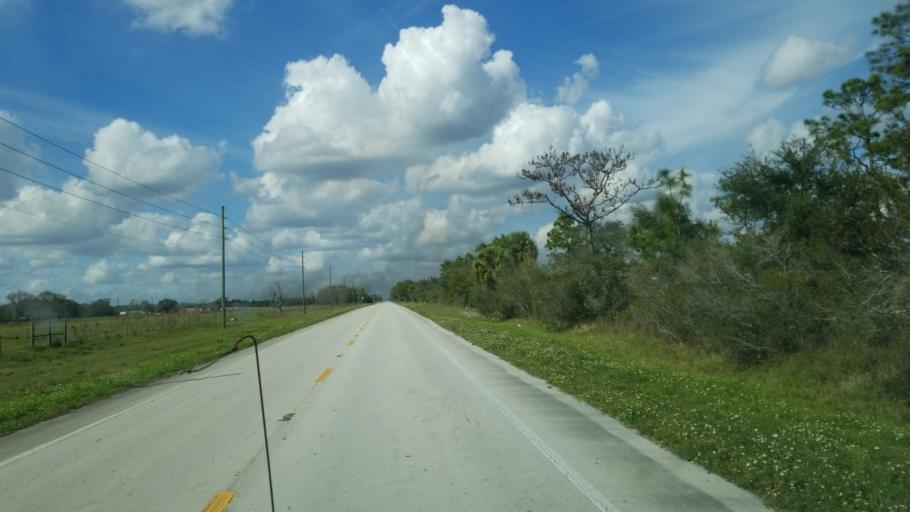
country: US
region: Florida
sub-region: Osceola County
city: Saint Cloud
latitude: 28.0320
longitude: -81.0412
